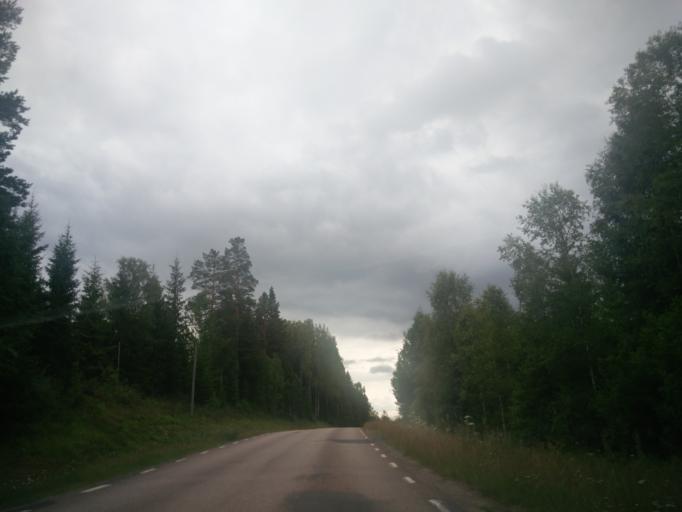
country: SE
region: Vaermland
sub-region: Arvika Kommun
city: Arvika
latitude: 59.9329
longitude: 12.6669
